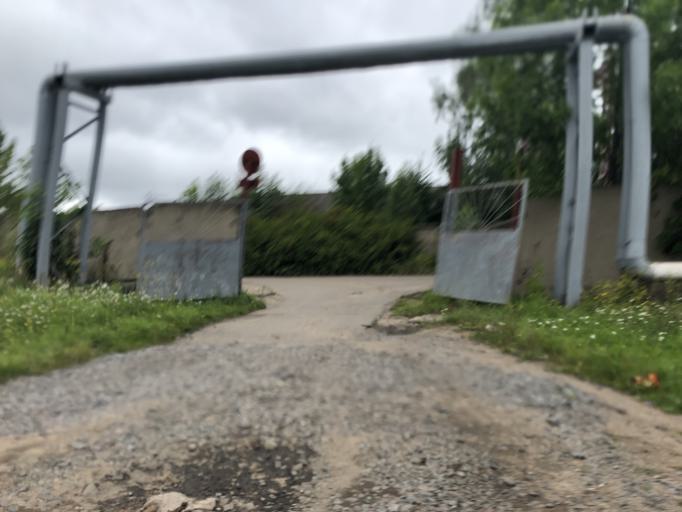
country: RU
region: Tverskaya
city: Rzhev
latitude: 56.2400
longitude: 34.3329
